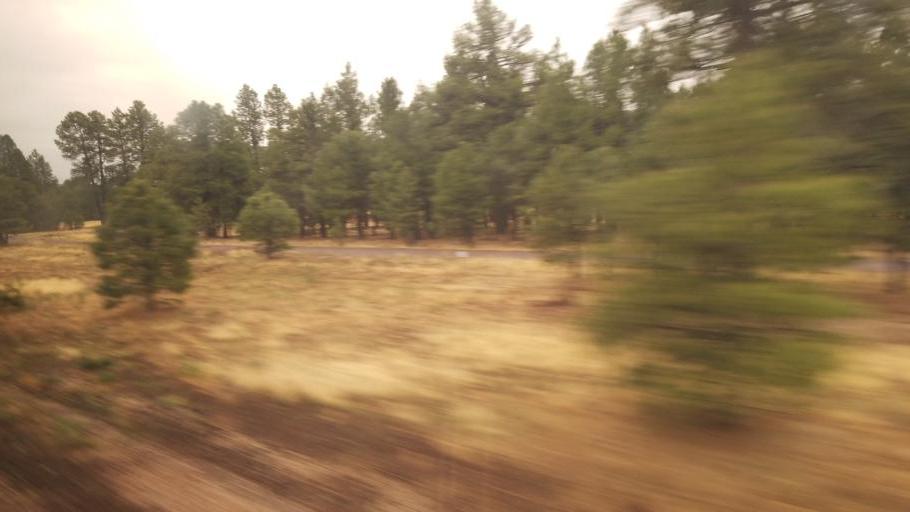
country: US
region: Arizona
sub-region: Coconino County
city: Parks
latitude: 35.2429
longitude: -111.8659
